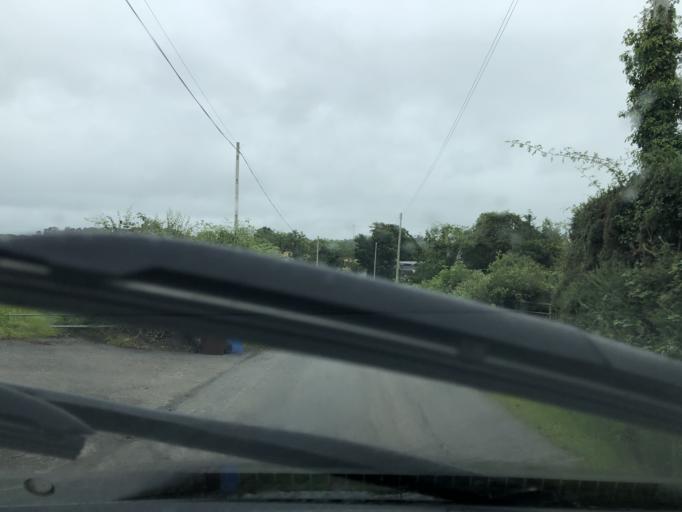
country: GB
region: Northern Ireland
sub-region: Down District
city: Dundrum
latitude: 54.3025
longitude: -5.8521
